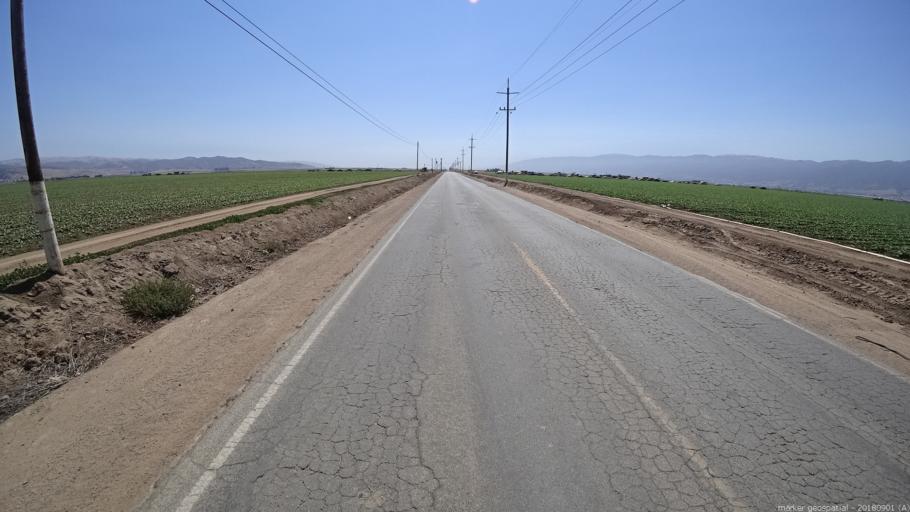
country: US
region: California
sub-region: Monterey County
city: Chualar
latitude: 36.6158
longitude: -121.5221
